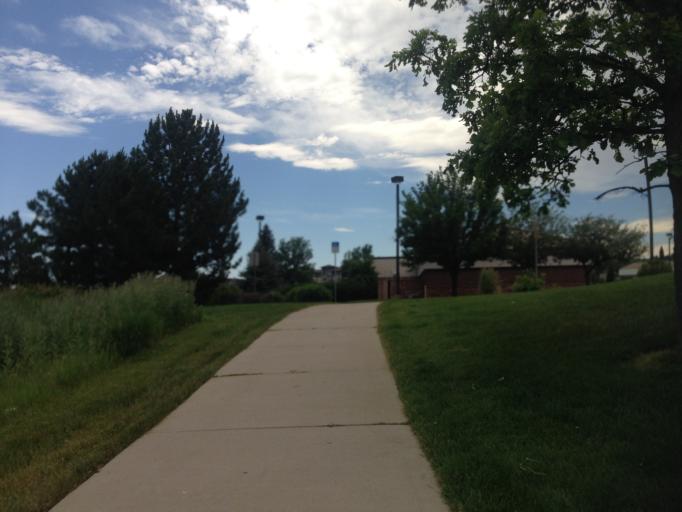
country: US
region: Colorado
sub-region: Boulder County
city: Superior
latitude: 39.9307
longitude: -105.1483
